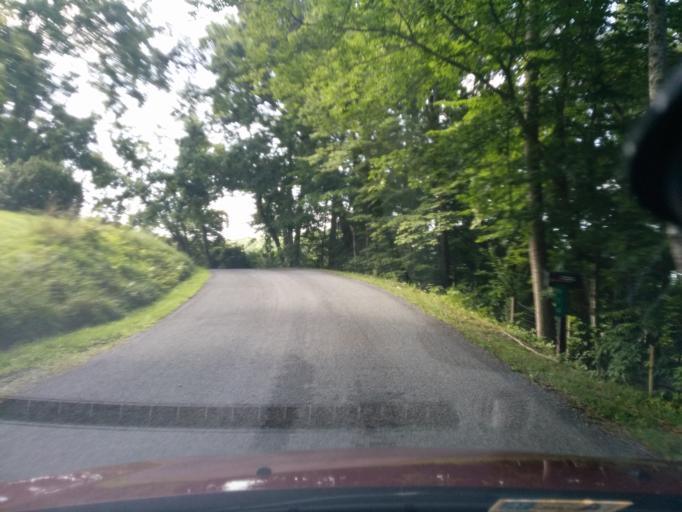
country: US
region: Virginia
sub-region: City of Lexington
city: Lexington
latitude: 37.7764
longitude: -79.4941
